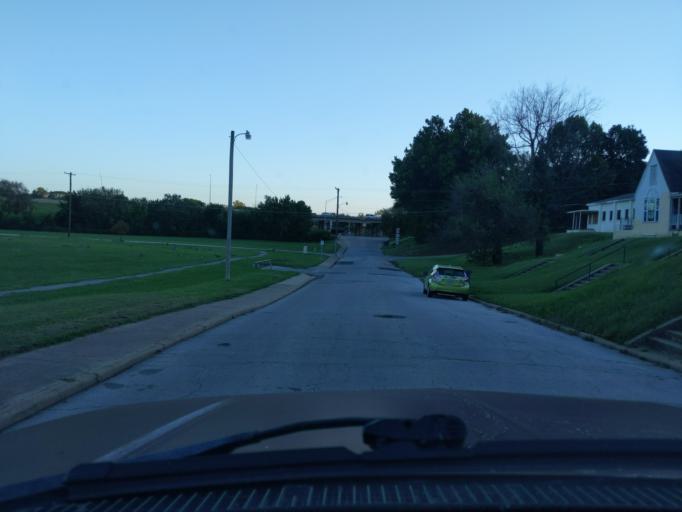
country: US
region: Oklahoma
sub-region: Tulsa County
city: Tulsa
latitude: 36.1584
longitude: -96.0071
